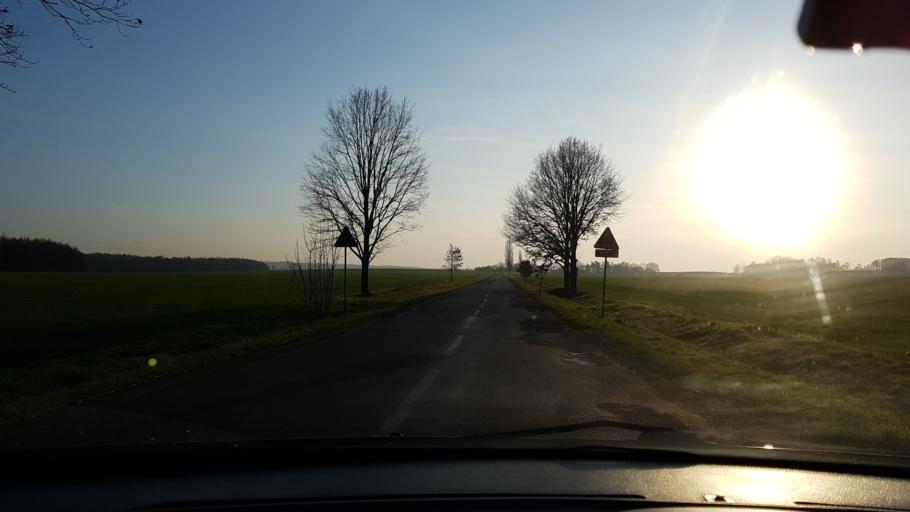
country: PL
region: Lower Silesian Voivodeship
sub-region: Powiat strzelinski
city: Przeworno
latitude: 50.6540
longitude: 17.2342
